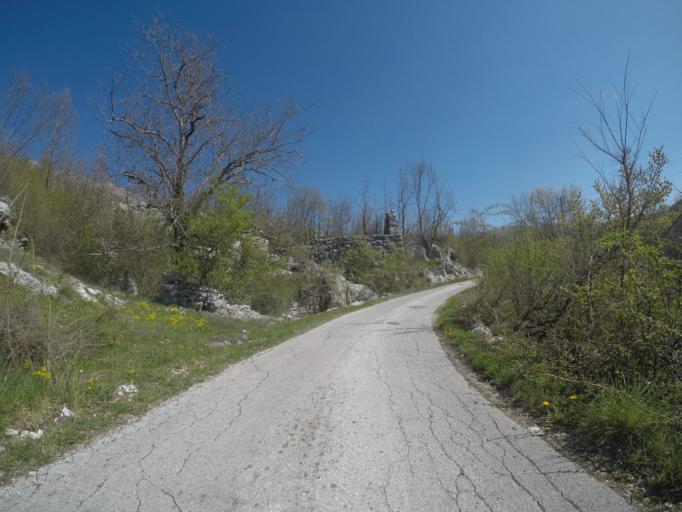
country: ME
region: Cetinje
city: Cetinje
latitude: 42.5329
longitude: 18.9766
